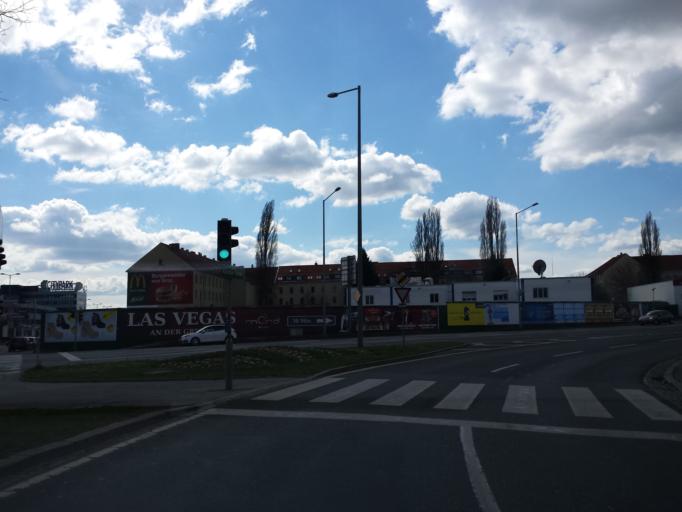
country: AT
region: Styria
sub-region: Graz Stadt
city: Wetzelsdorf
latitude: 47.0629
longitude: 15.4235
